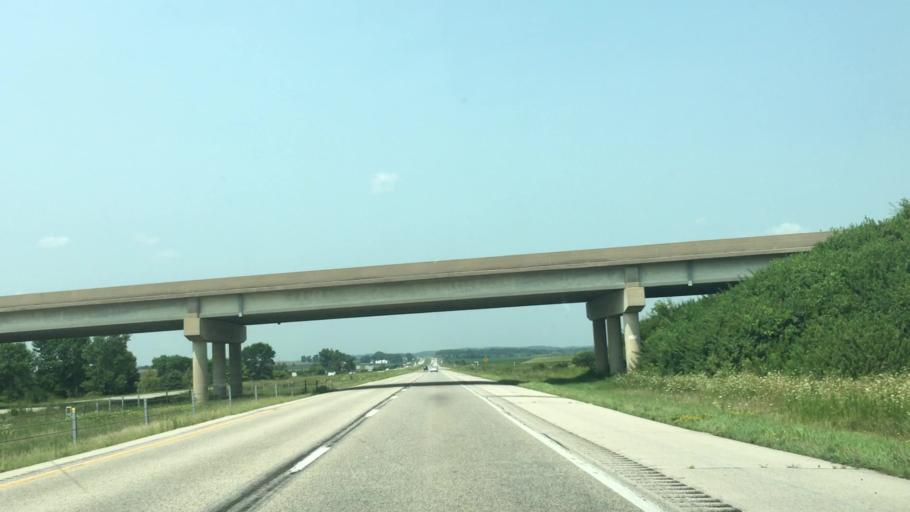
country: US
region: Iowa
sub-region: Linn County
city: Center Point
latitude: 42.1705
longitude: -91.7790
